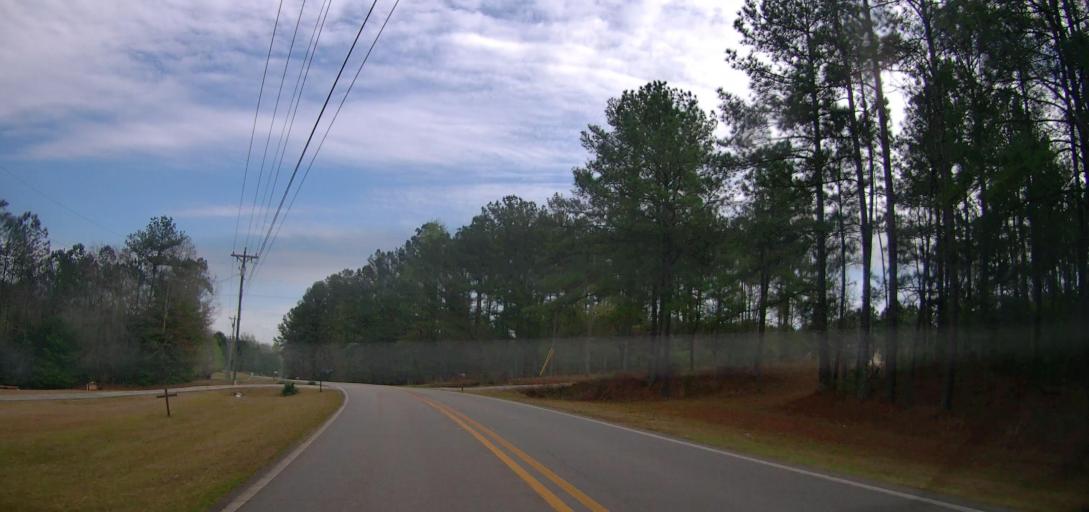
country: US
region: Georgia
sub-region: Bibb County
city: Macon
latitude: 32.9570
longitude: -83.6567
